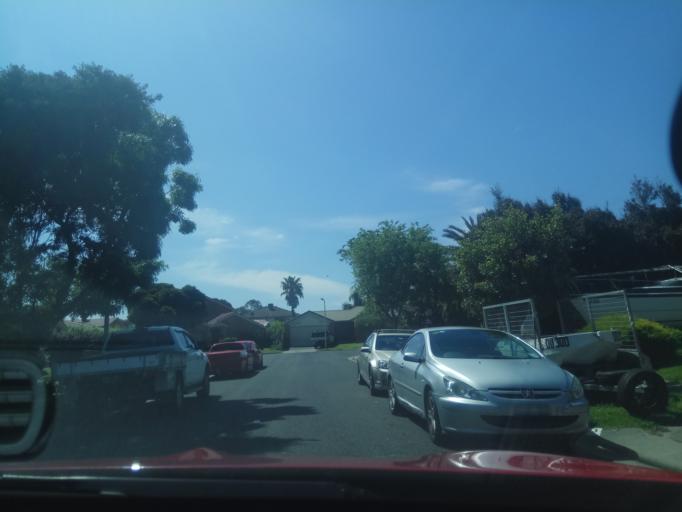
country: AU
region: Victoria
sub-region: Kingston
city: Aspendale Gardens
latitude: -38.0244
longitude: 145.1175
